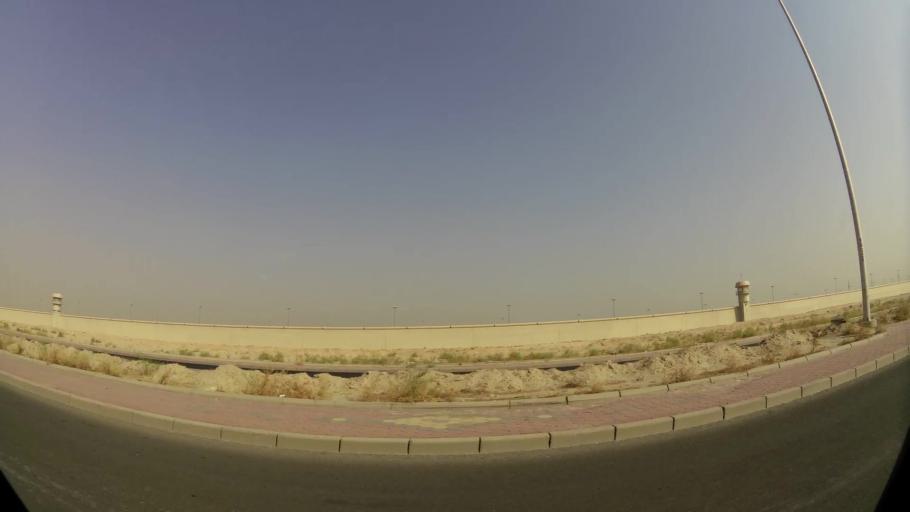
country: KW
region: Al Asimah
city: Ar Rabiyah
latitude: 29.2747
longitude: 47.8592
